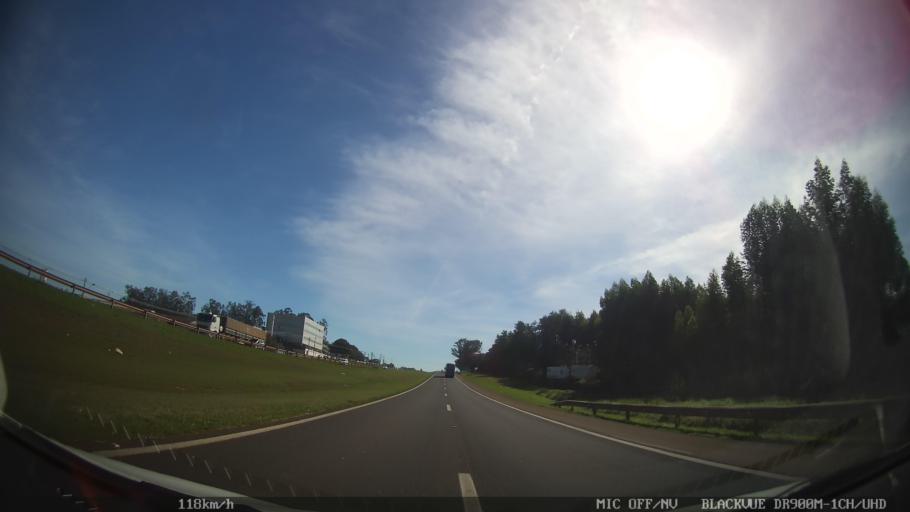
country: BR
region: Sao Paulo
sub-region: Leme
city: Leme
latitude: -22.2088
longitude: -47.3943
